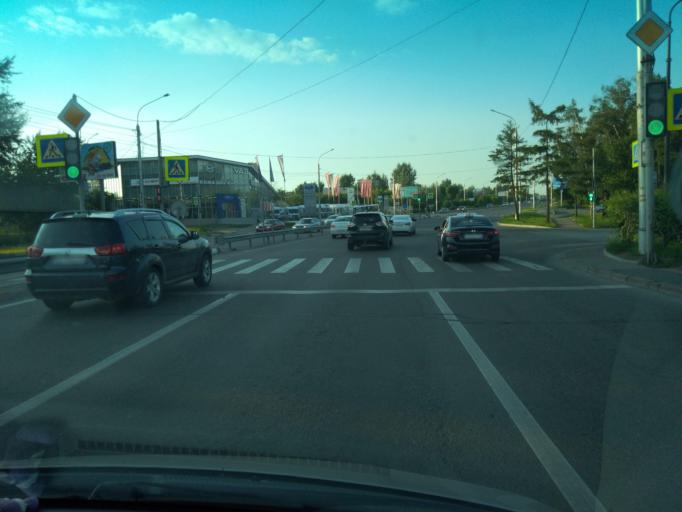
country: RU
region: Krasnoyarskiy
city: Krasnoyarsk
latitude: 56.0233
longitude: 92.8853
